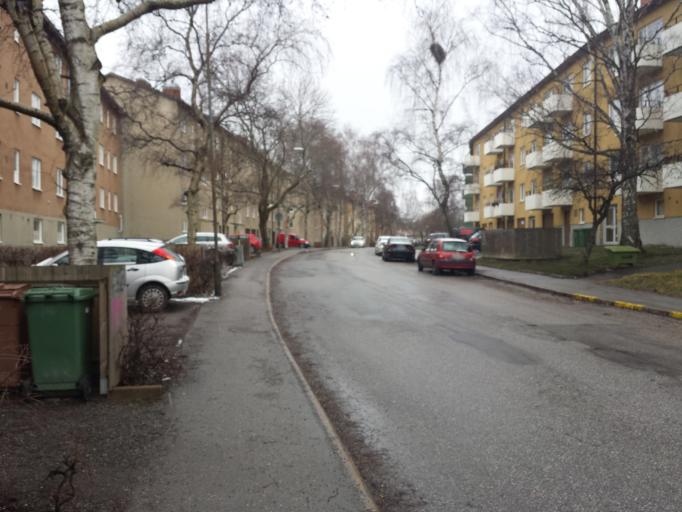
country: SE
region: Stockholm
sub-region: Nacka Kommun
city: Nacka
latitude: 59.2895
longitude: 18.1117
